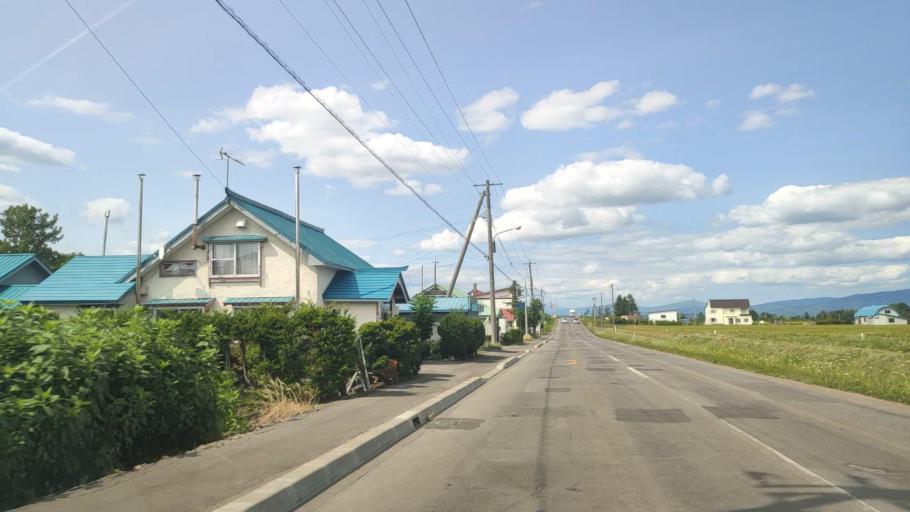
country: JP
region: Hokkaido
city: Nayoro
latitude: 44.2965
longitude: 142.4294
